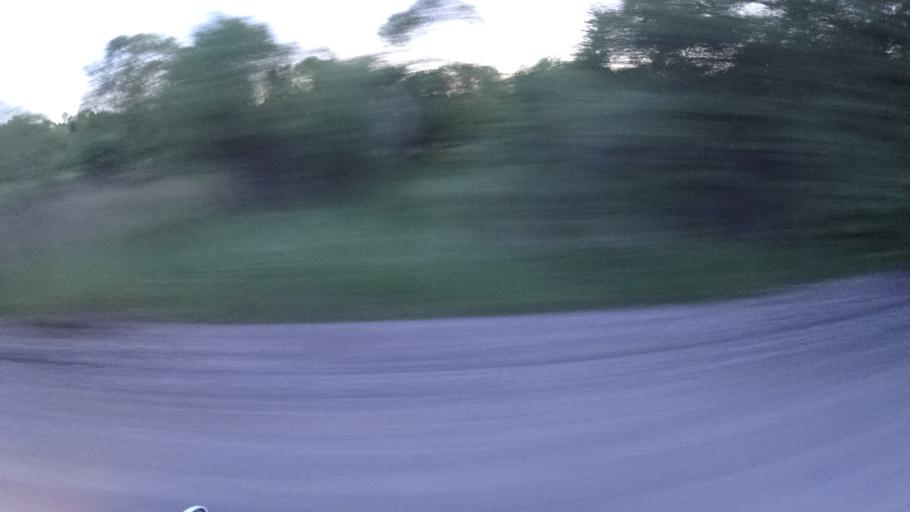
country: RU
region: Khabarovsk Krai
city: Khor
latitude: 47.8484
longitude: 134.9457
